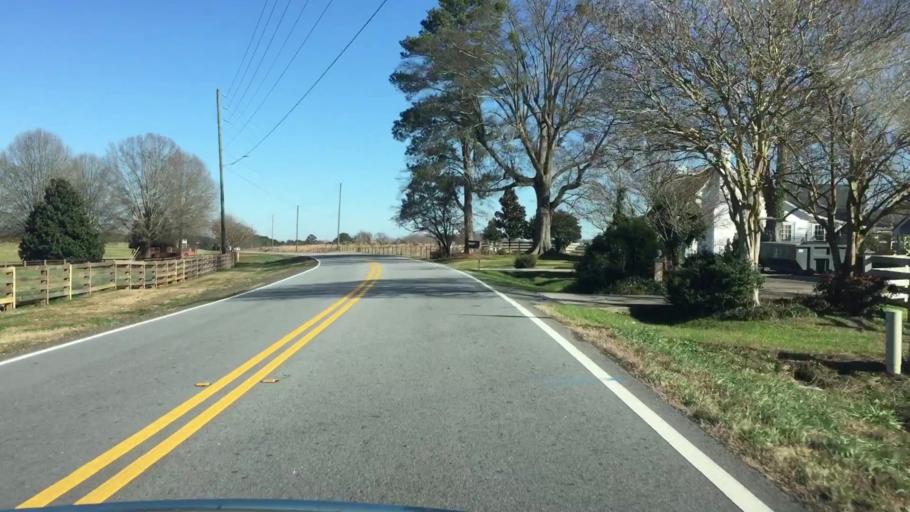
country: US
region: Georgia
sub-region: Henry County
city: McDonough
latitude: 33.5002
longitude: -84.0876
